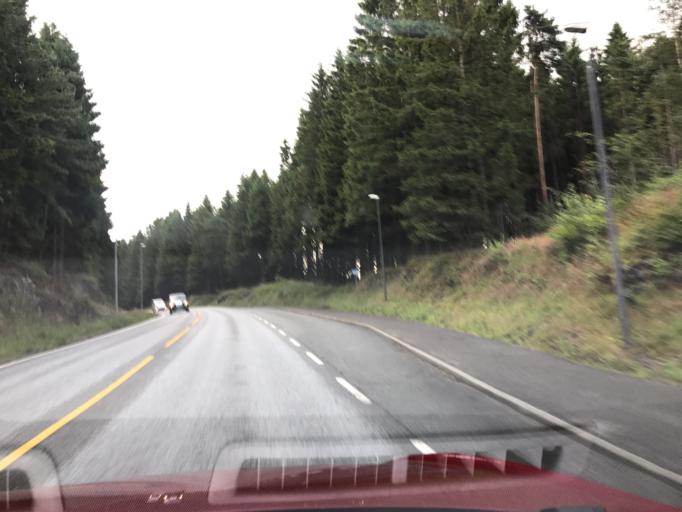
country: NO
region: Hordaland
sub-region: Stord
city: Leirvik
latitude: 59.7667
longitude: 5.4680
